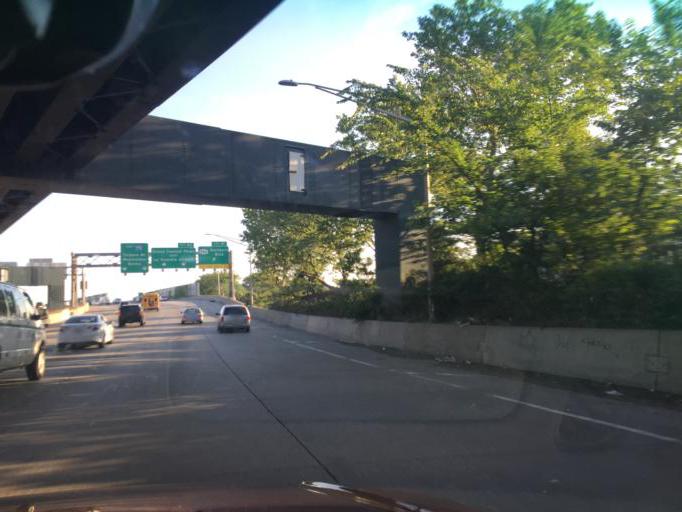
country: US
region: New York
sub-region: Queens County
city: Long Island City
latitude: 40.7512
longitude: -73.8972
